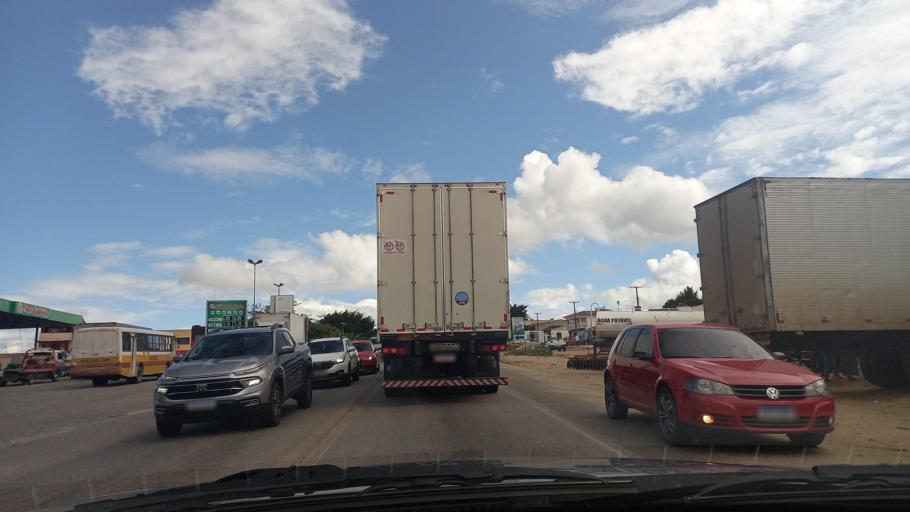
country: BR
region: Pernambuco
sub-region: Lajedo
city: Lajedo
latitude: -8.7098
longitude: -36.4193
